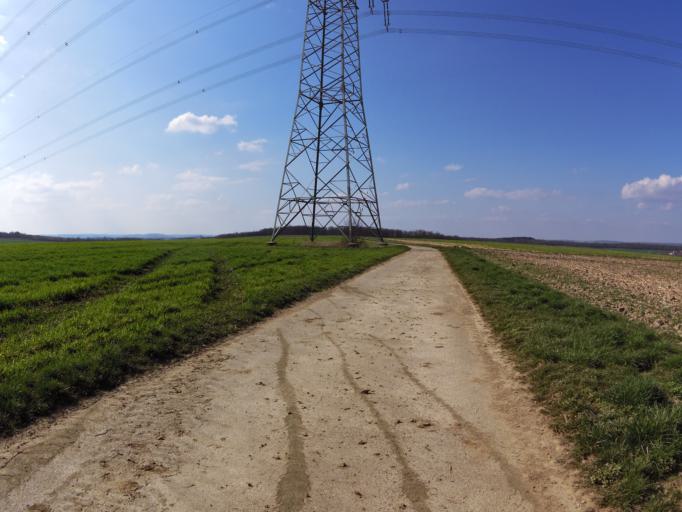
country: DE
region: Bavaria
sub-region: Regierungsbezirk Unterfranken
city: Rottendorf
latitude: 49.8015
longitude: 10.0680
